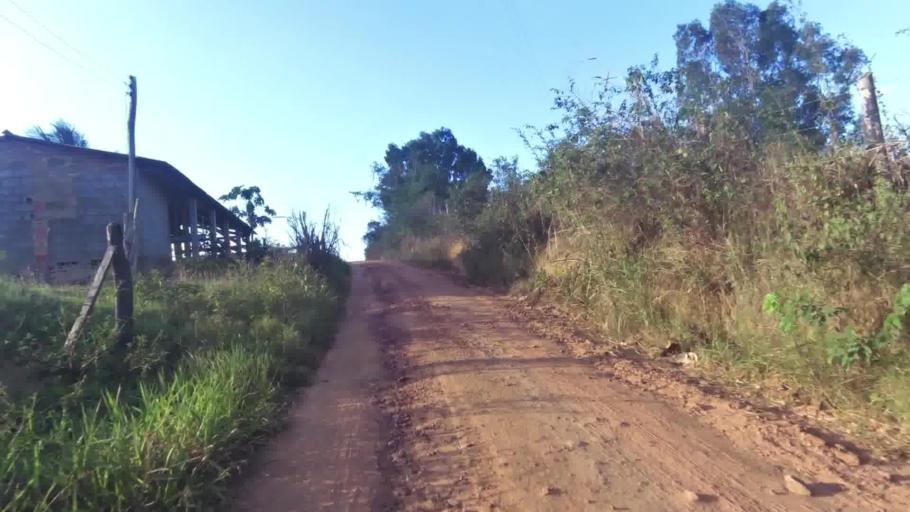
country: BR
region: Espirito Santo
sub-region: Marataizes
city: Marataizes
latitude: -21.1623
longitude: -41.0369
